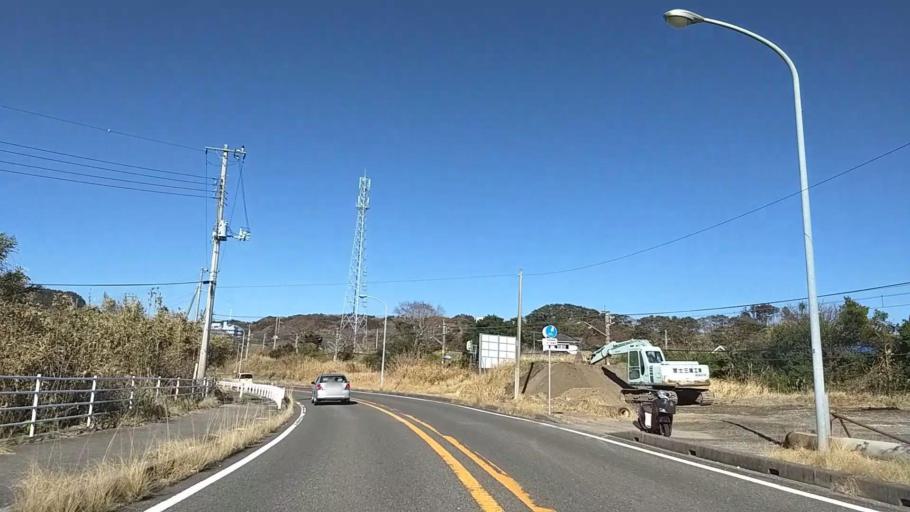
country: JP
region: Chiba
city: Kawaguchi
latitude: 35.0847
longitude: 140.0950
